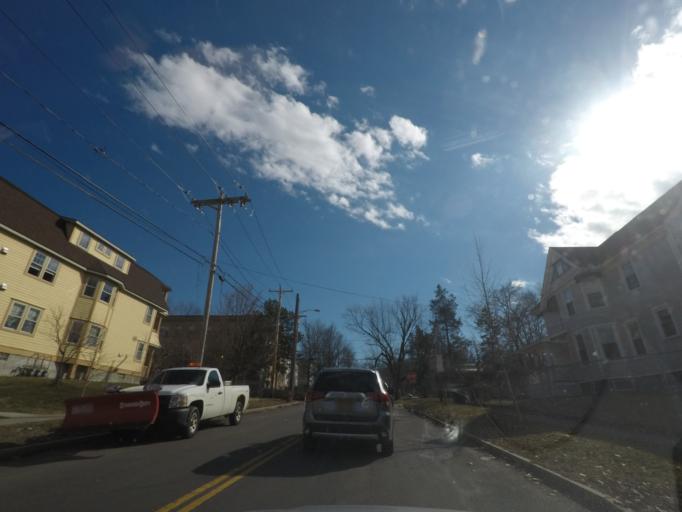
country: US
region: New York
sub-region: Onondaga County
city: Syracuse
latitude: 43.0475
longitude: -76.1214
